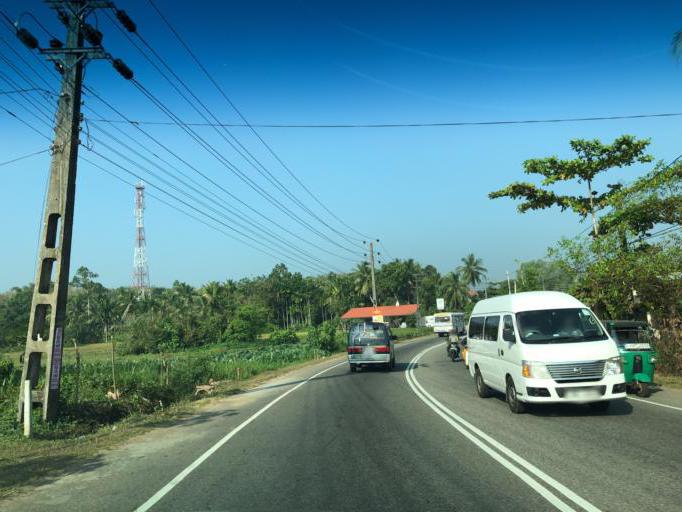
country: LK
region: Western
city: Horana South
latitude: 6.7235
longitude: 80.0893
